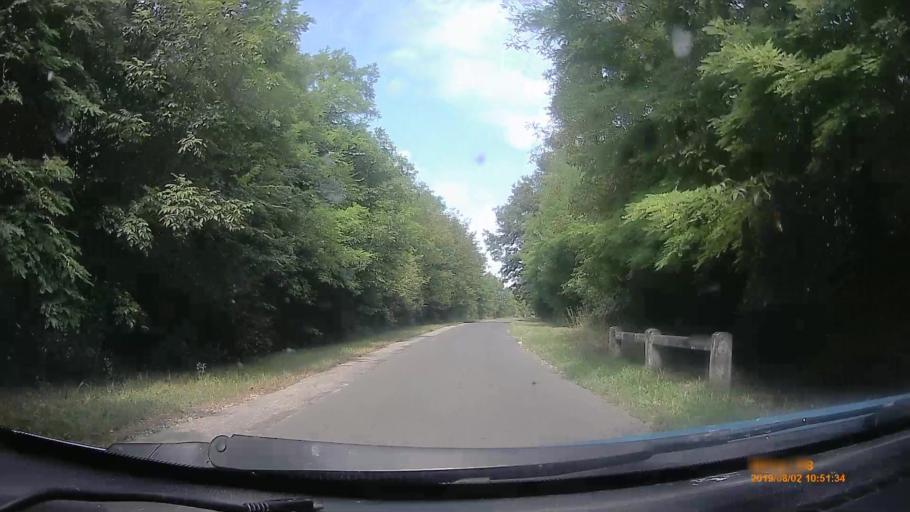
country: HU
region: Baranya
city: Buekkoesd
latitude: 46.0863
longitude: 17.9670
